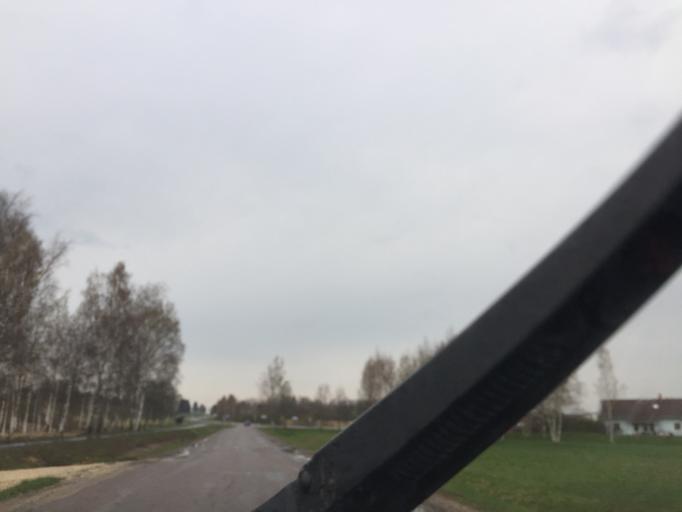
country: EE
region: Tartu
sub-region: UElenurme vald
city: Ulenurme
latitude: 58.3040
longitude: 26.7241
